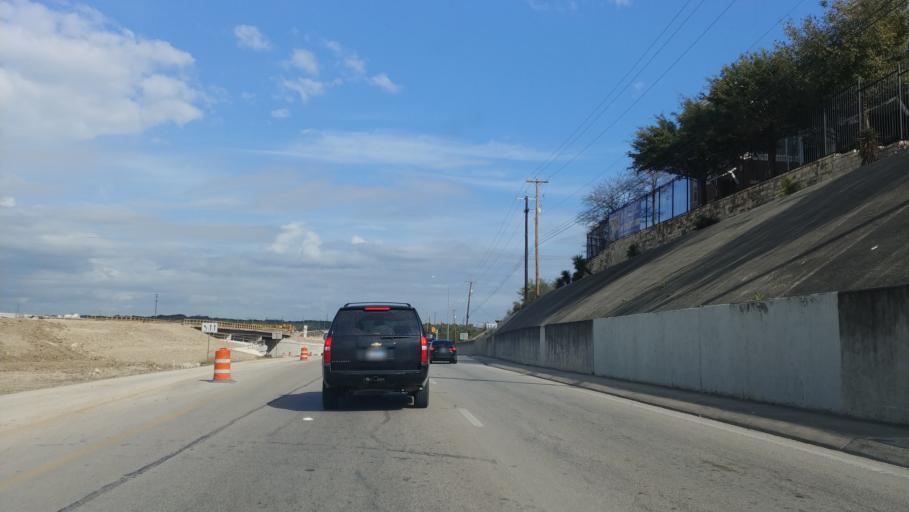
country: US
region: Texas
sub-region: Bexar County
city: Leon Valley
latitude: 29.4635
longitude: -98.7109
